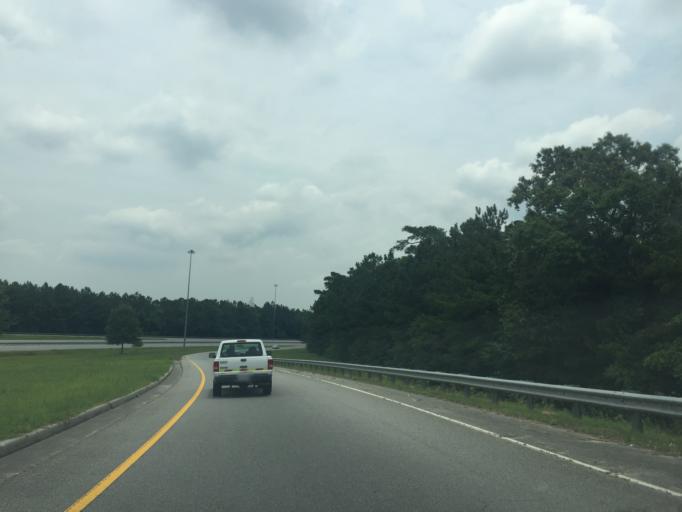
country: US
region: Georgia
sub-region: Chatham County
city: Garden City
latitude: 32.0391
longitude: -81.1627
